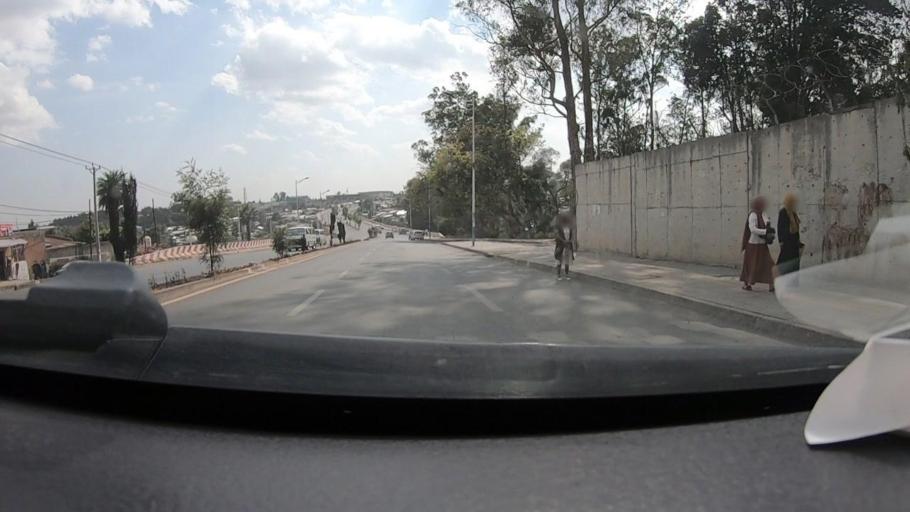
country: ET
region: Adis Abeba
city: Addis Ababa
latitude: 9.0515
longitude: 38.7708
